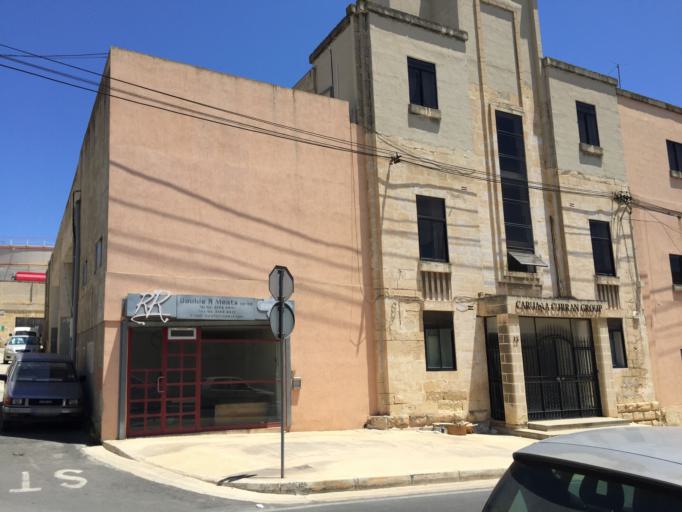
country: MT
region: Il-Marsa
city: Marsa
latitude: 35.8864
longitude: 14.4989
